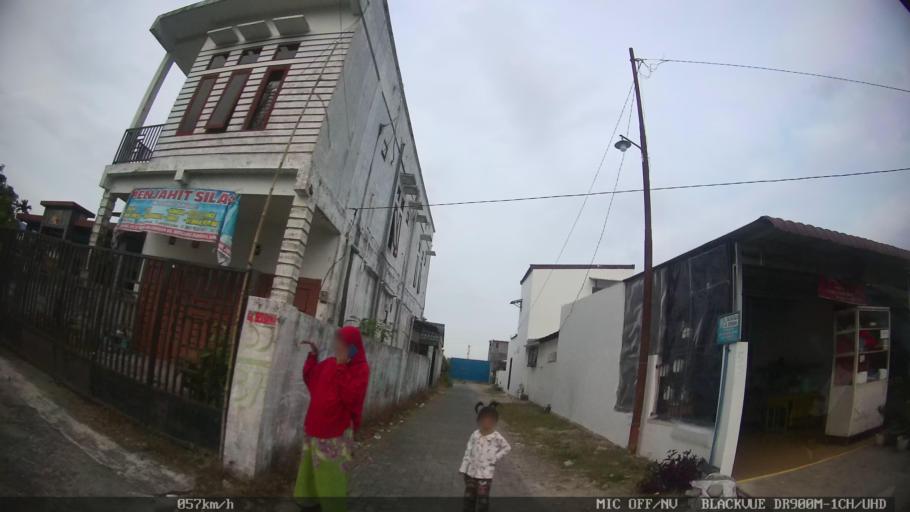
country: ID
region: North Sumatra
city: Sunggal
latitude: 3.5736
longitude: 98.6048
